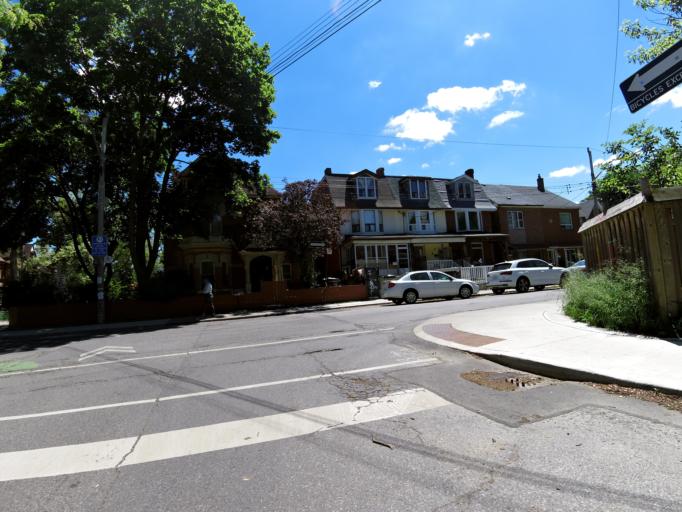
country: CA
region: Ontario
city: Toronto
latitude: 43.6532
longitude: -79.4029
